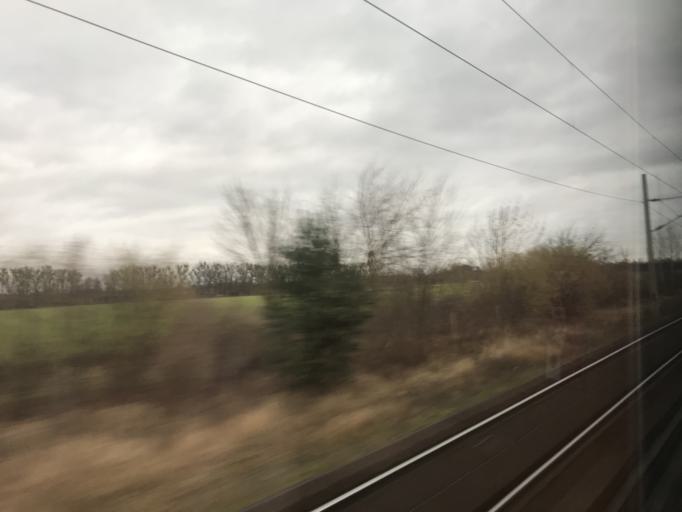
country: DE
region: Brandenburg
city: Dallgow-Doeberitz
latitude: 52.5428
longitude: 13.0725
